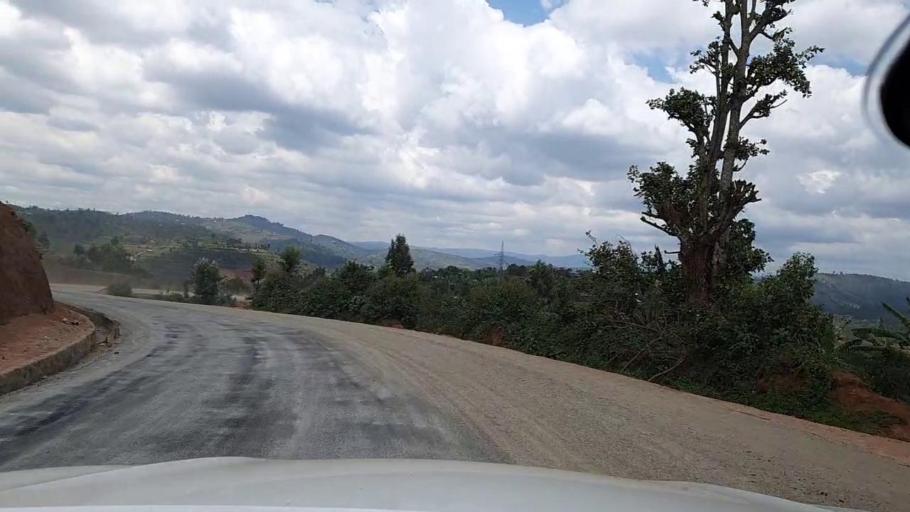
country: RW
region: Southern Province
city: Butare
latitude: -2.6981
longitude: 29.5642
